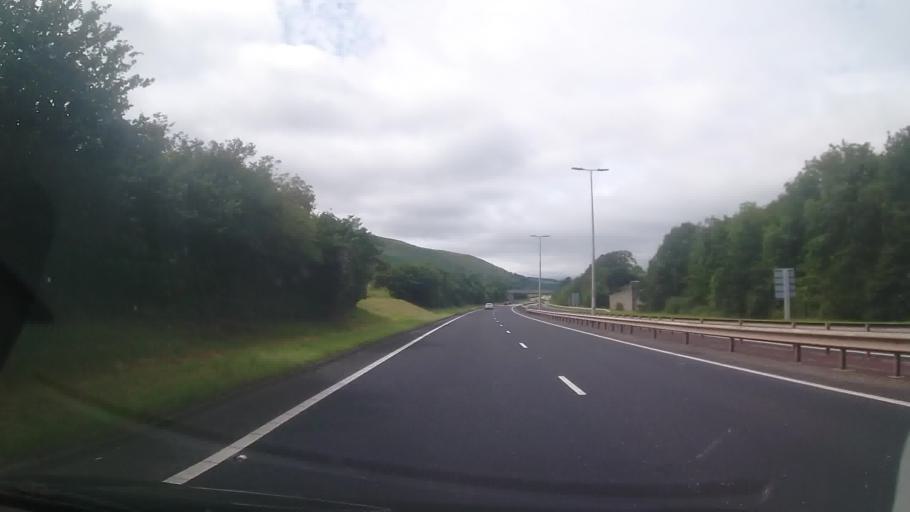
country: GB
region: Wales
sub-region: Gwynedd
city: Aber
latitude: 53.2424
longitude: -4.0005
